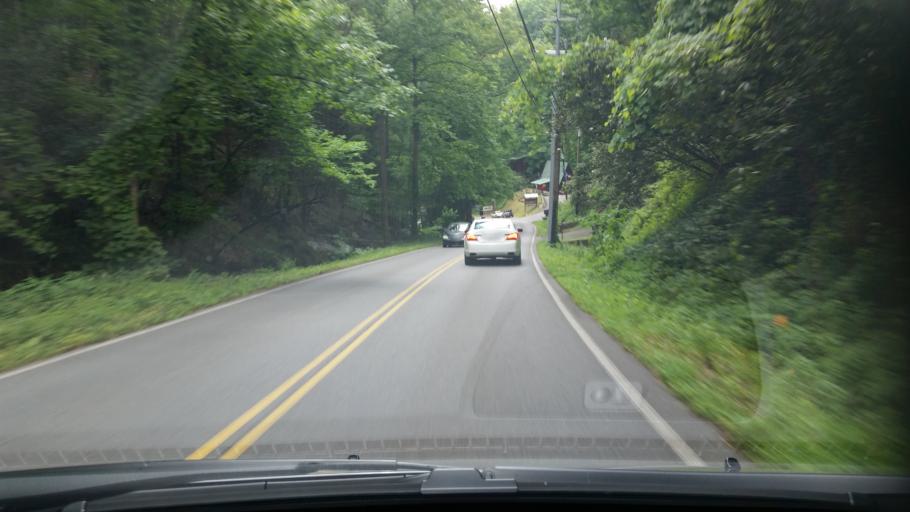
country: US
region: Tennessee
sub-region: Sevier County
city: Gatlinburg
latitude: 35.7105
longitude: -83.5424
